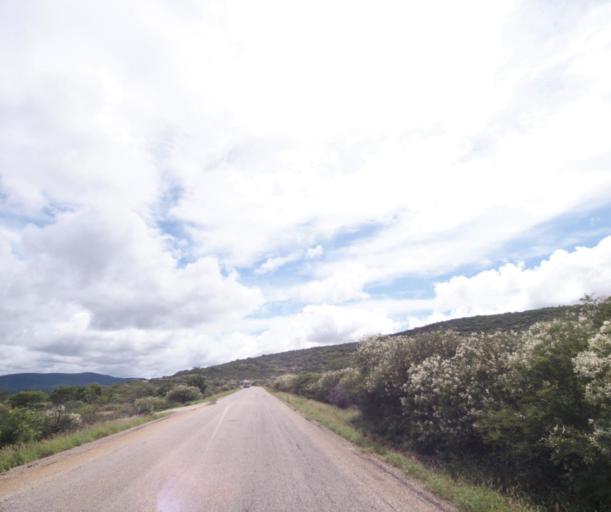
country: BR
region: Bahia
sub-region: Brumado
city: Brumado
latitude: -14.2057
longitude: -41.6220
